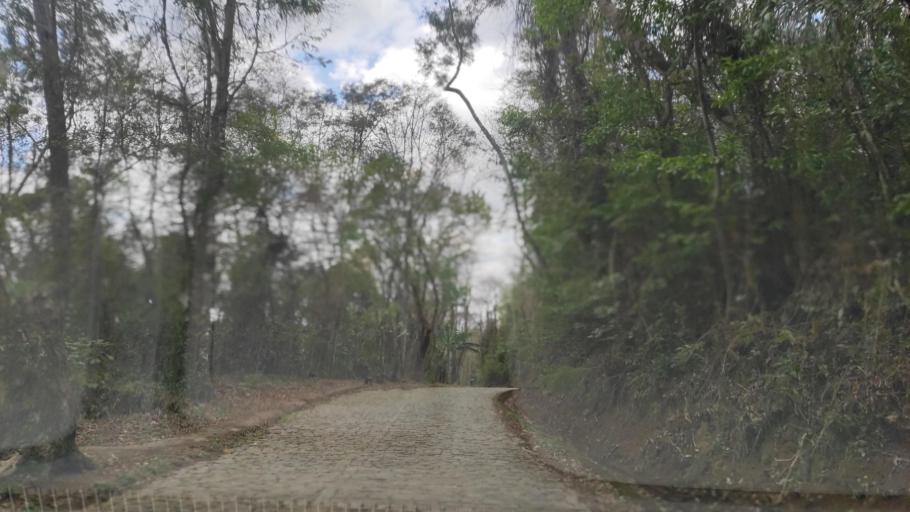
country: BR
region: Espirito Santo
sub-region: Vitoria
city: Vitoria
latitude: -20.3038
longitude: -40.3397
